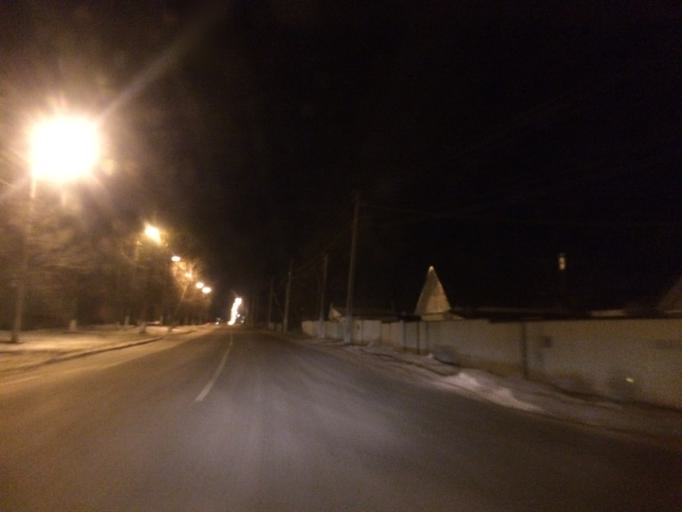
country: RU
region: Tula
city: Tula
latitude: 54.1820
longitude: 37.7094
